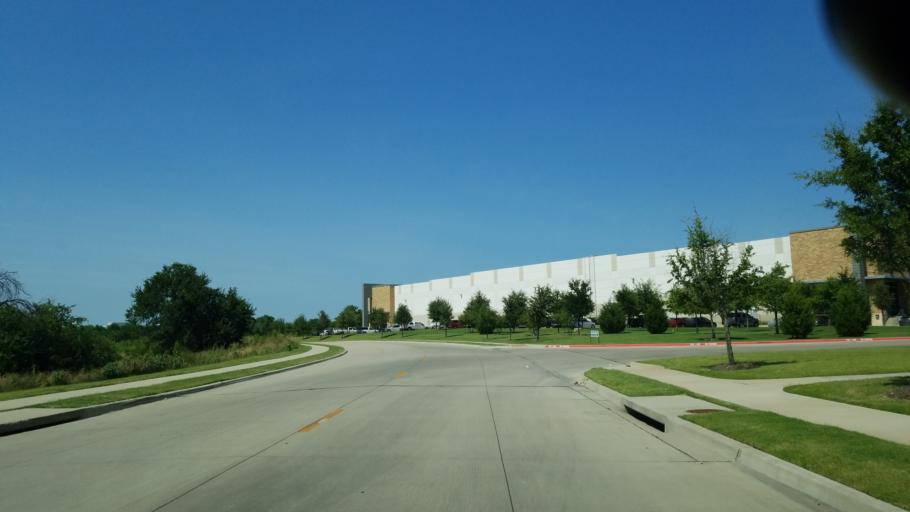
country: US
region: Texas
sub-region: Dallas County
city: Farmers Branch
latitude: 32.9119
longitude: -96.9041
